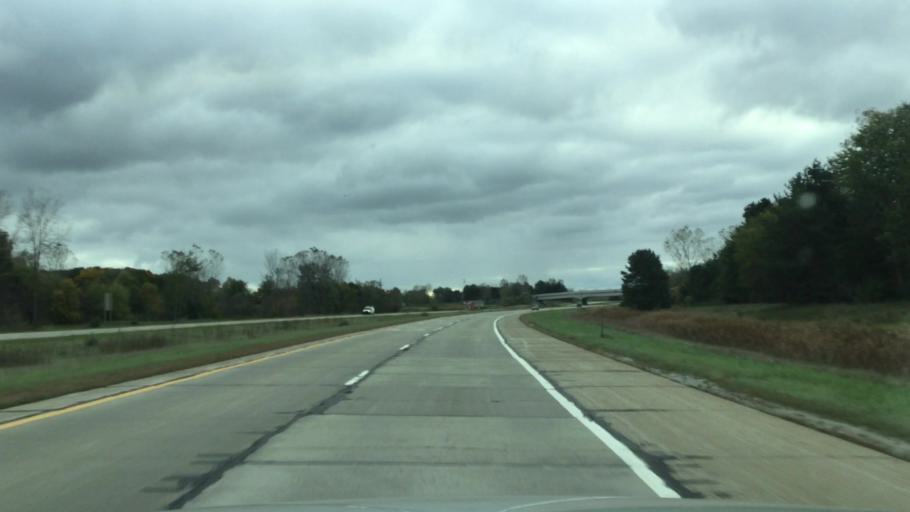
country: US
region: Michigan
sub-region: Saint Clair County
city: Capac
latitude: 42.9866
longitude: -82.8589
